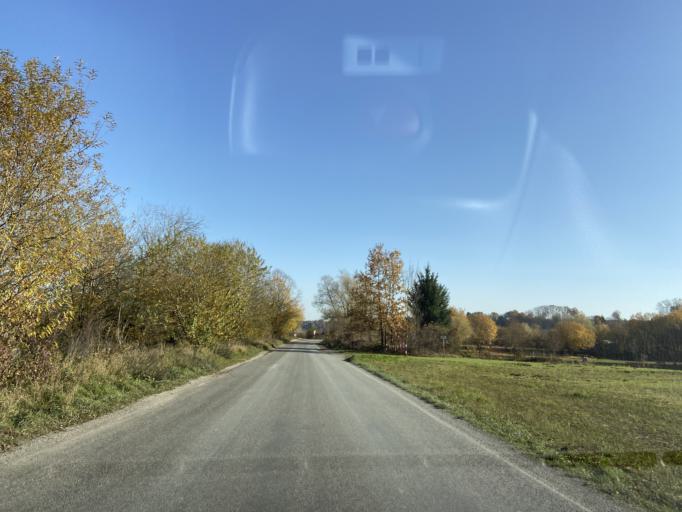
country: DE
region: Baden-Wuerttemberg
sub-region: Tuebingen Region
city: Krauchenwies
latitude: 48.0330
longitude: 9.2717
